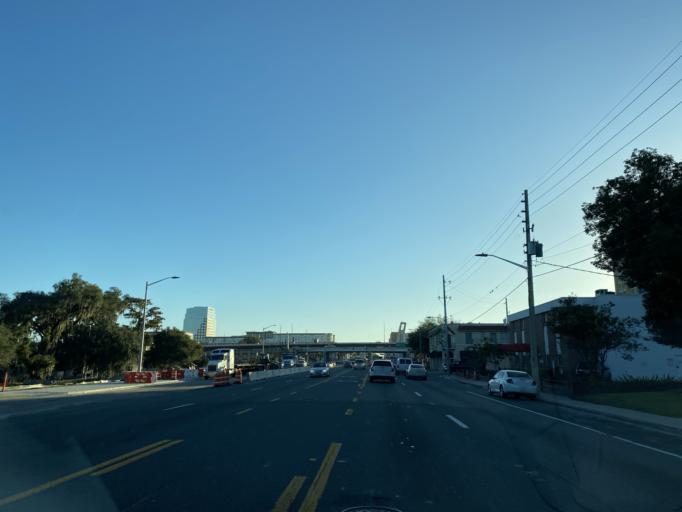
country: US
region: Florida
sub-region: Orange County
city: Orlando
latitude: 28.5530
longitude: -81.3850
